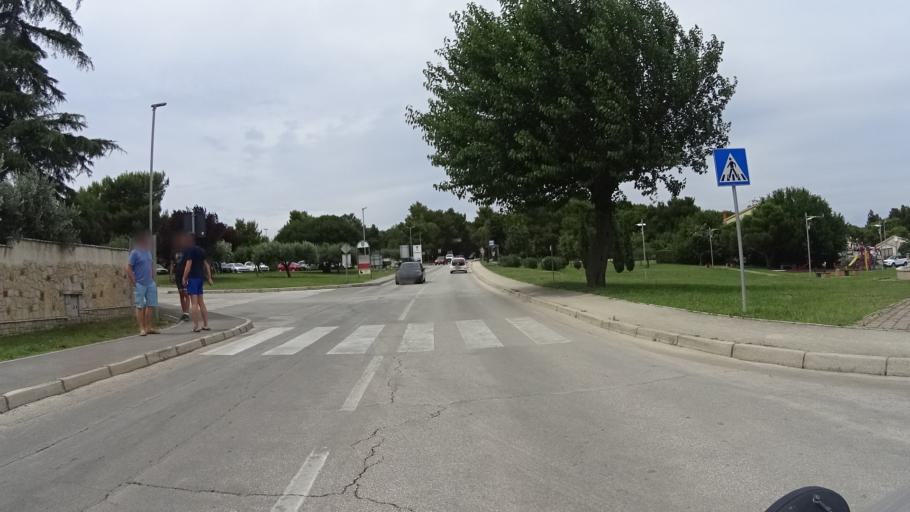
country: HR
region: Istarska
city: Medulin
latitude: 44.8050
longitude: 13.9096
